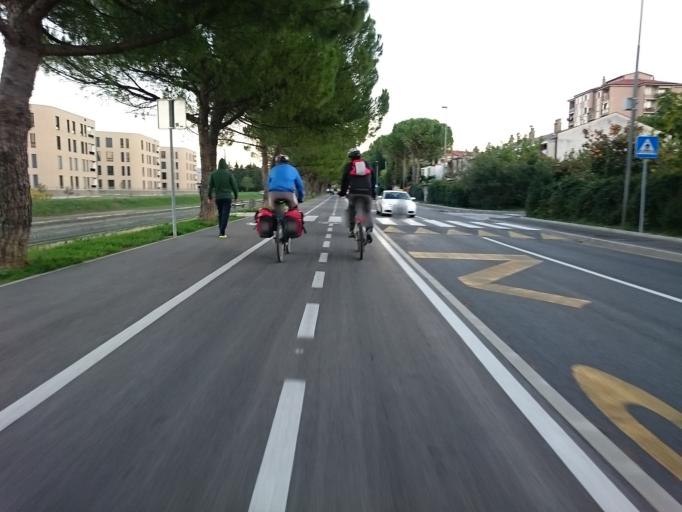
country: SI
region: Koper-Capodistria
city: Koper
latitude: 45.5373
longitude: 13.7275
